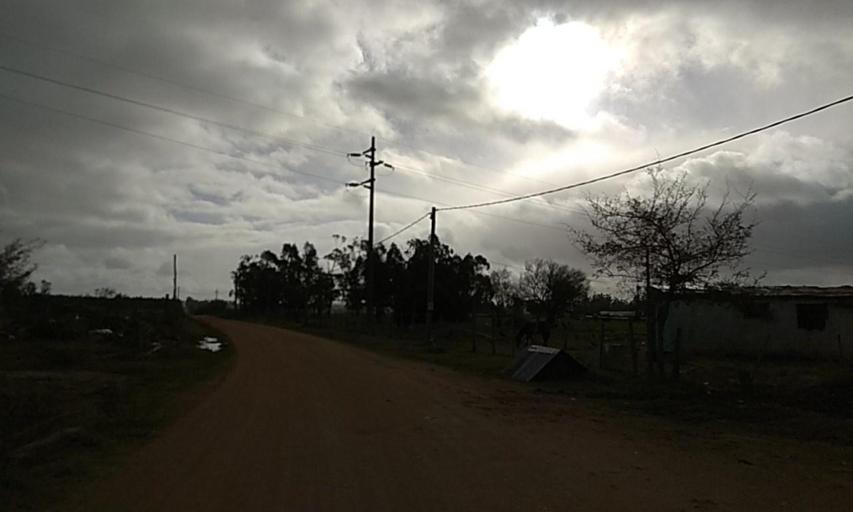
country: UY
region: Florida
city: Florida
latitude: -34.0743
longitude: -56.2335
